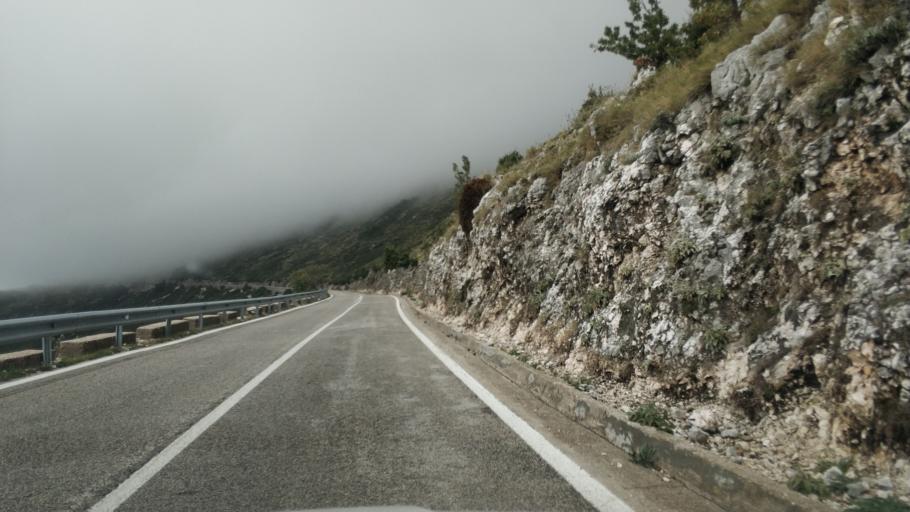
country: AL
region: Vlore
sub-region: Rrethi i Vlores
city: Vranisht
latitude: 40.1907
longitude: 19.6084
